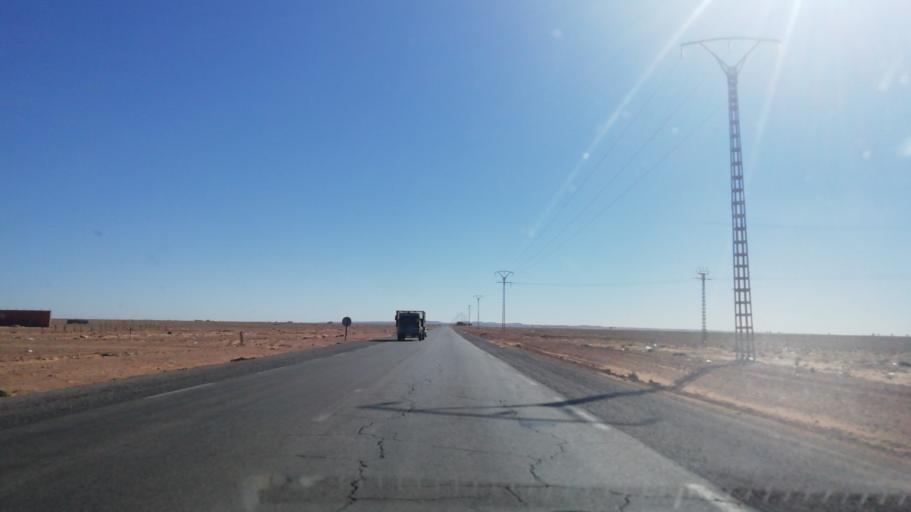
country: DZ
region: Saida
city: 'Ain el Hadjar
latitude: 34.0193
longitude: 0.1059
